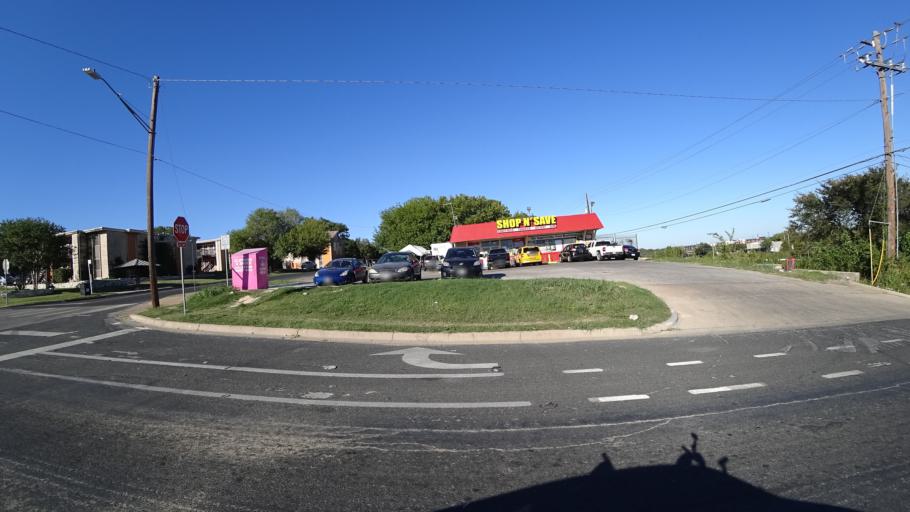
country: US
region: Texas
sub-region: Travis County
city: Austin
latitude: 30.2358
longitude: -97.7283
